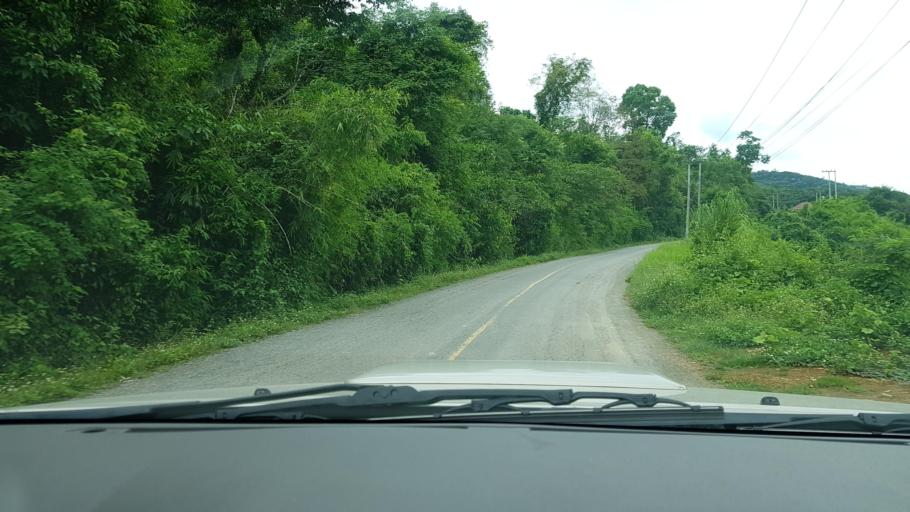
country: LA
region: Loungnamtha
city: Muang Nale
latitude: 20.2312
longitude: 101.5637
